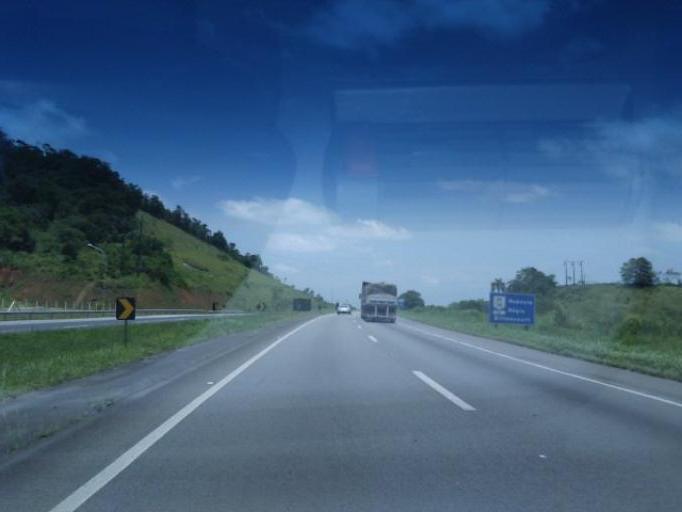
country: BR
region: Sao Paulo
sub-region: Miracatu
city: Miracatu
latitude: -24.2915
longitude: -47.4683
